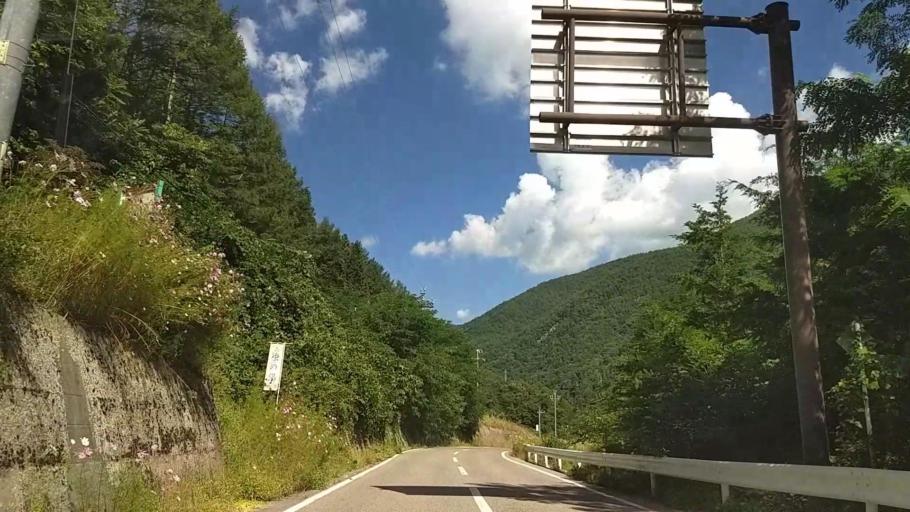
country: JP
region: Nagano
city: Matsumoto
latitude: 36.1970
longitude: 138.0644
